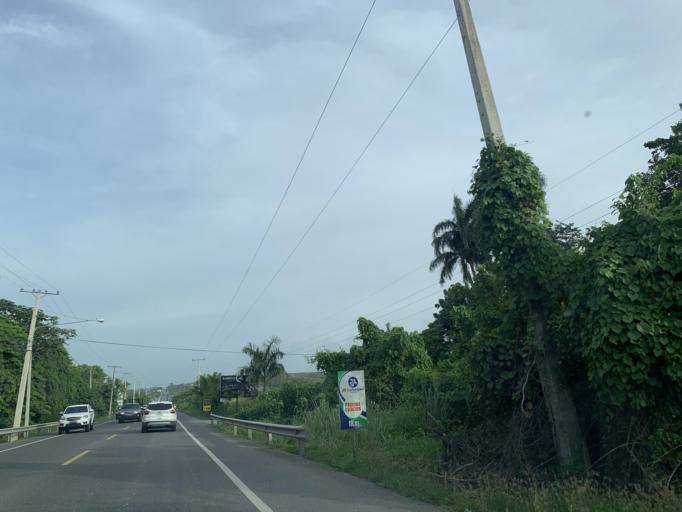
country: DO
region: Puerto Plata
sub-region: Puerto Plata
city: Puerto Plata
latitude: 19.7480
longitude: -70.6382
